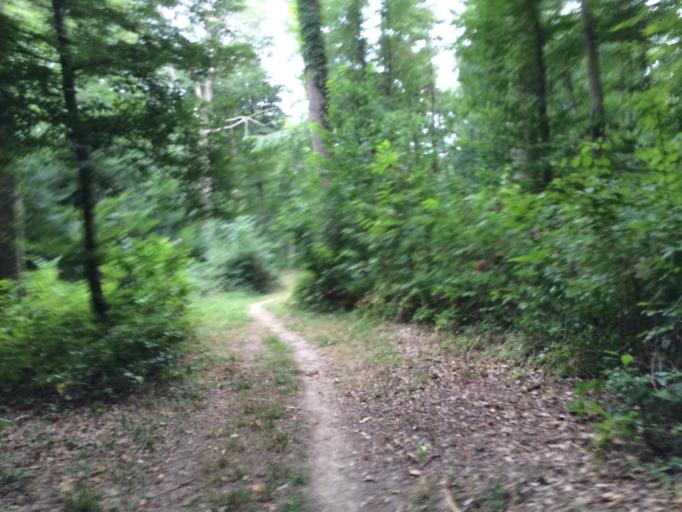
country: FR
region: Ile-de-France
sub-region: Departement de l'Essonne
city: Quincy-sous-Senart
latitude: 48.6535
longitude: 2.5340
